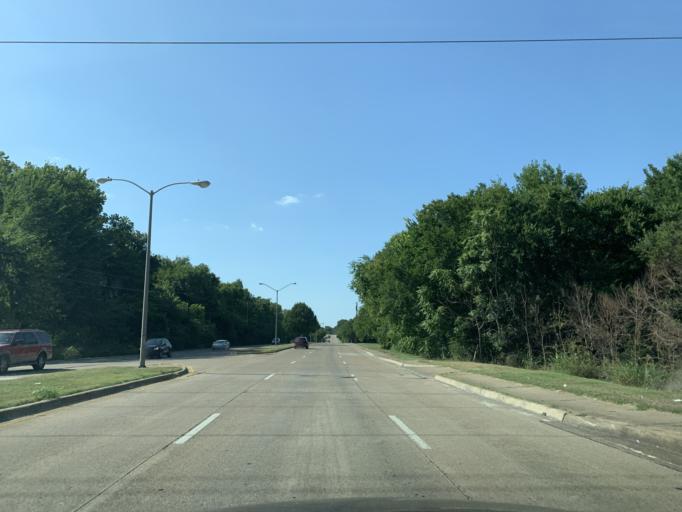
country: US
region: Texas
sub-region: Dallas County
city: Hutchins
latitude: 32.6837
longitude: -96.7680
